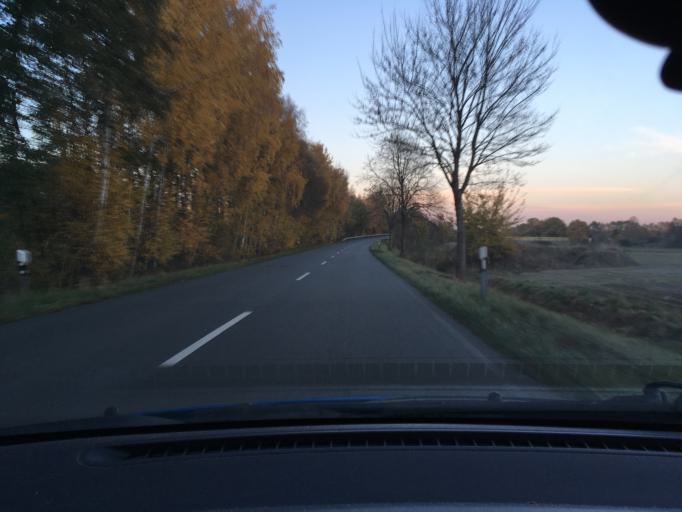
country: DE
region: Lower Saxony
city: Radbruch
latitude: 53.3159
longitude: 10.2812
